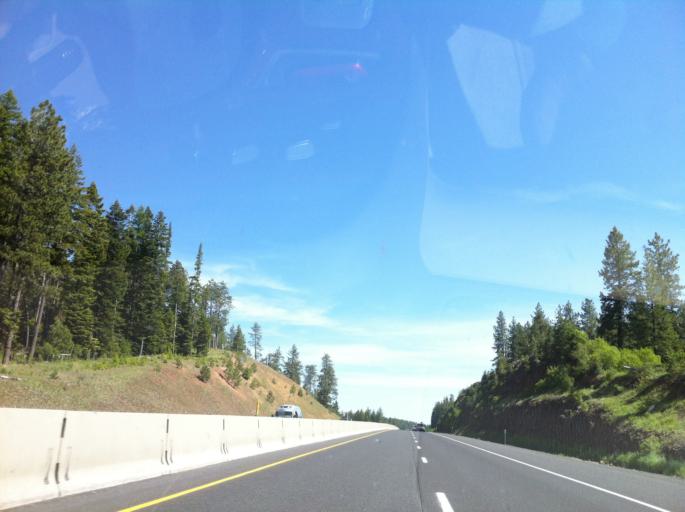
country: US
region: Oregon
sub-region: Umatilla County
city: Mission
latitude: 45.4809
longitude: -118.4027
